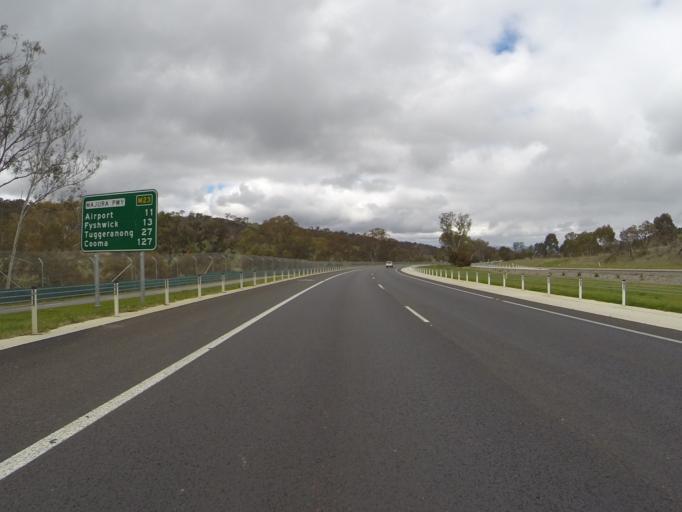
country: AU
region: Australian Capital Territory
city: Kaleen
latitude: -35.2177
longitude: 149.1954
